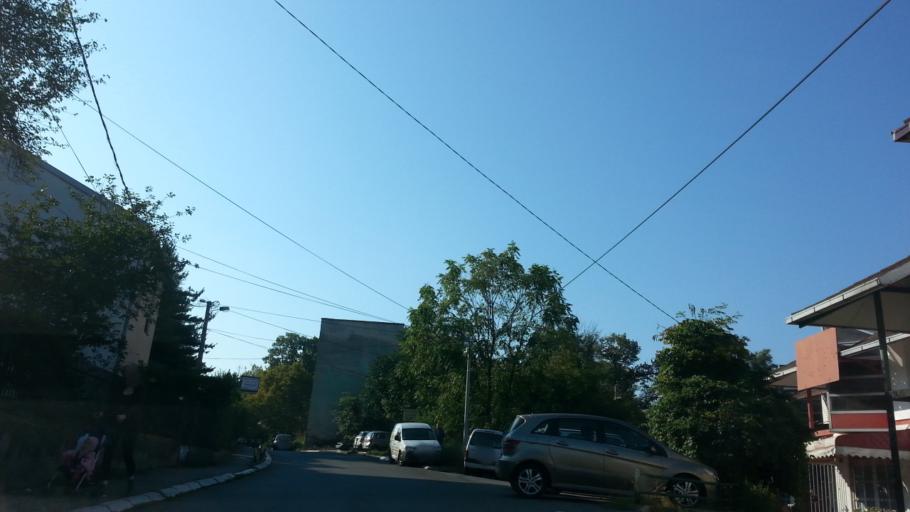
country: RS
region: Central Serbia
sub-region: Belgrade
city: Cukarica
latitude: 44.7702
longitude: 20.4143
